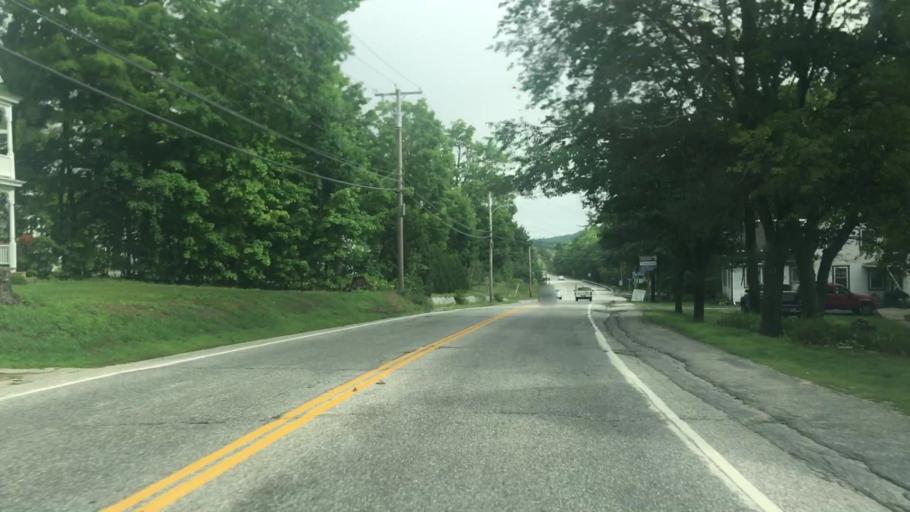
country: US
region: Maine
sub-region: Oxford County
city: South Paris
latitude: 44.2275
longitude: -70.5141
